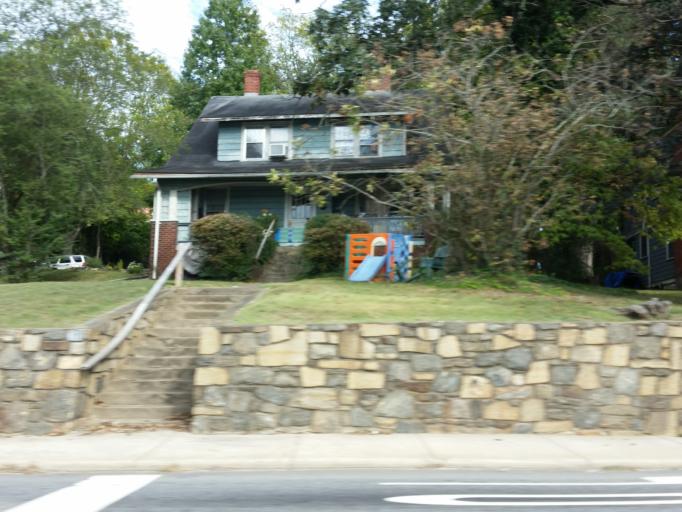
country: US
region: North Carolina
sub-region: Buncombe County
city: Asheville
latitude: 35.6056
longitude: -82.5531
